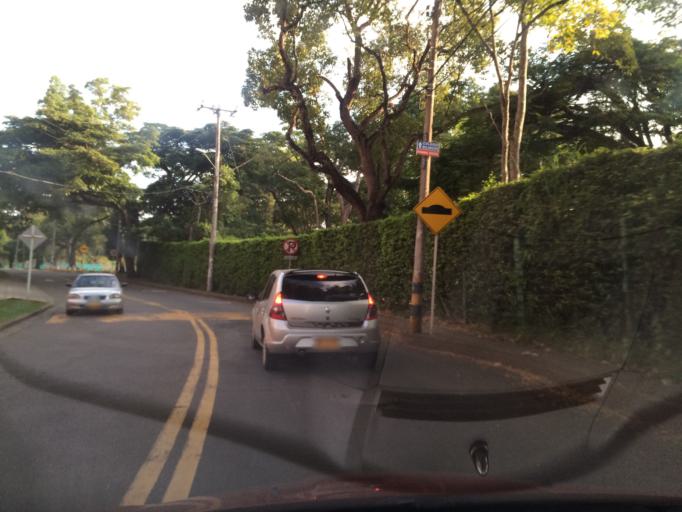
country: CO
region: Valle del Cauca
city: Cali
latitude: 3.3702
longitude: -76.5416
